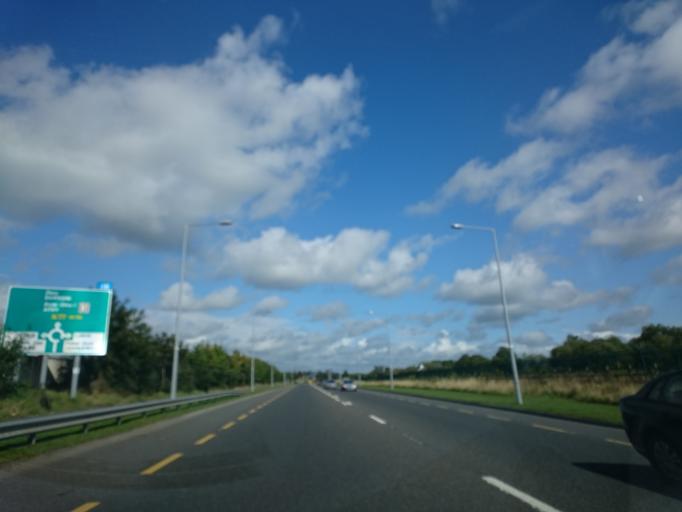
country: IE
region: Leinster
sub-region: Kilkenny
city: Kilkenny
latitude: 52.6618
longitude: -7.2268
